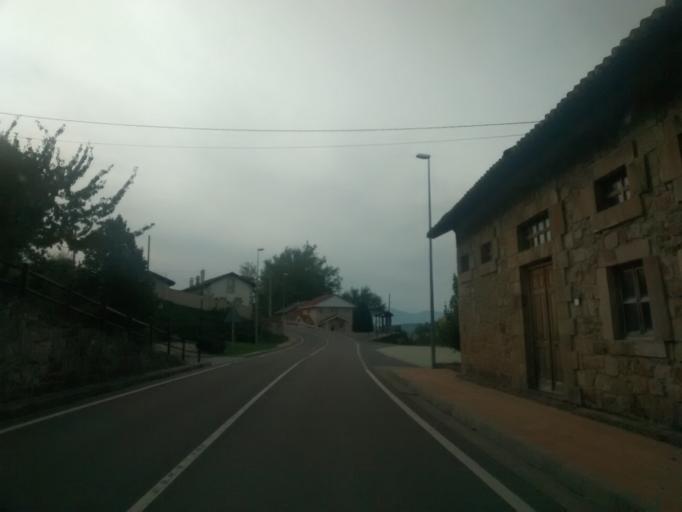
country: ES
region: Cantabria
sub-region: Provincia de Cantabria
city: San Miguel de Aguayo
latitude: 42.9733
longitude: -4.0292
